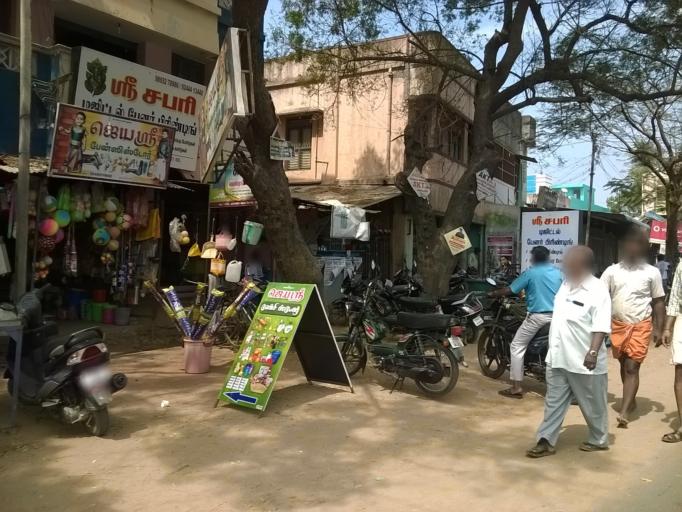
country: IN
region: Tamil Nadu
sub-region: Cuddalore
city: Panruti
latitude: 11.7688
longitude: 79.5502
